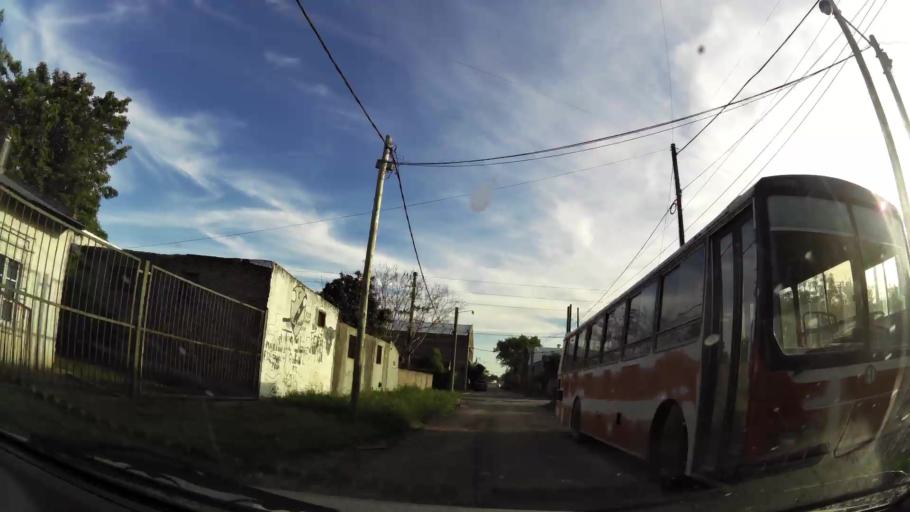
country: AR
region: Buenos Aires
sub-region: Partido de Almirante Brown
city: Adrogue
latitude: -34.7986
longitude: -58.3276
